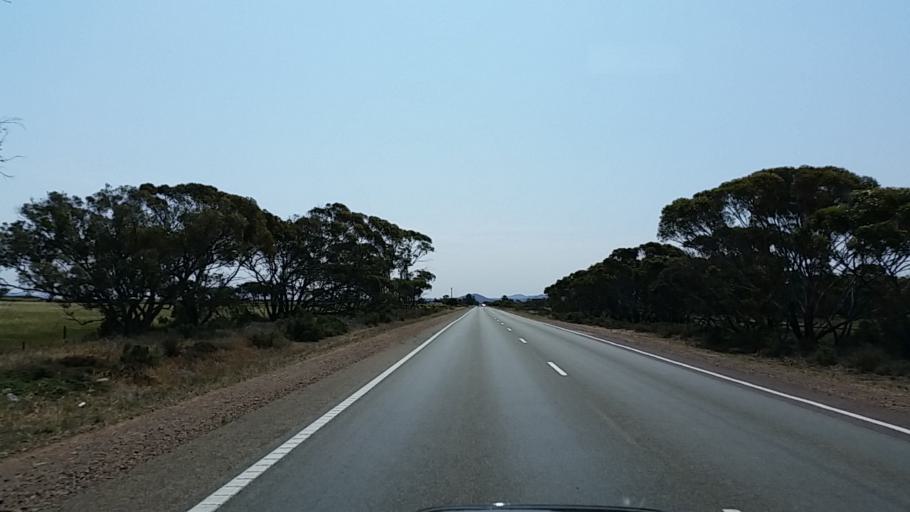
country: AU
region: South Australia
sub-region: Port Pirie City and Dists
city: Port Pirie
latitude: -32.9343
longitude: 137.9824
